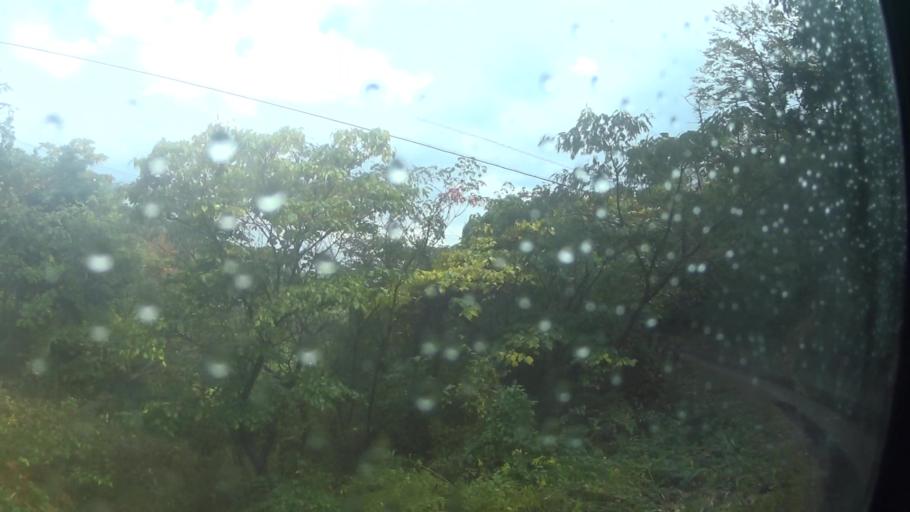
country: JP
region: Kyoto
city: Miyazu
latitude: 35.5860
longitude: 135.1924
